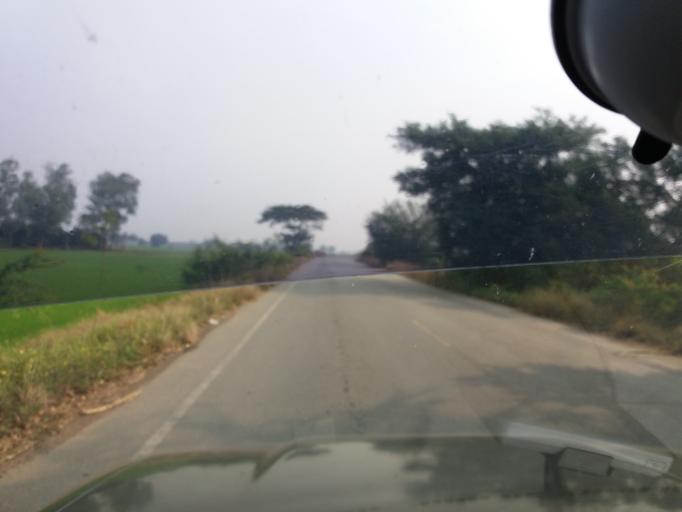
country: TH
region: Suphan Buri
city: Doem Bang Nang Buat
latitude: 14.8526
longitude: 100.1313
